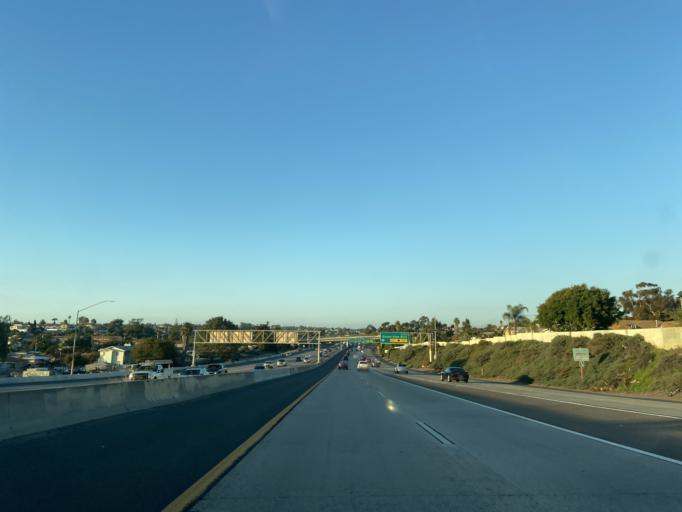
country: US
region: California
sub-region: San Diego County
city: National City
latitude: 32.6969
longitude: -117.1208
